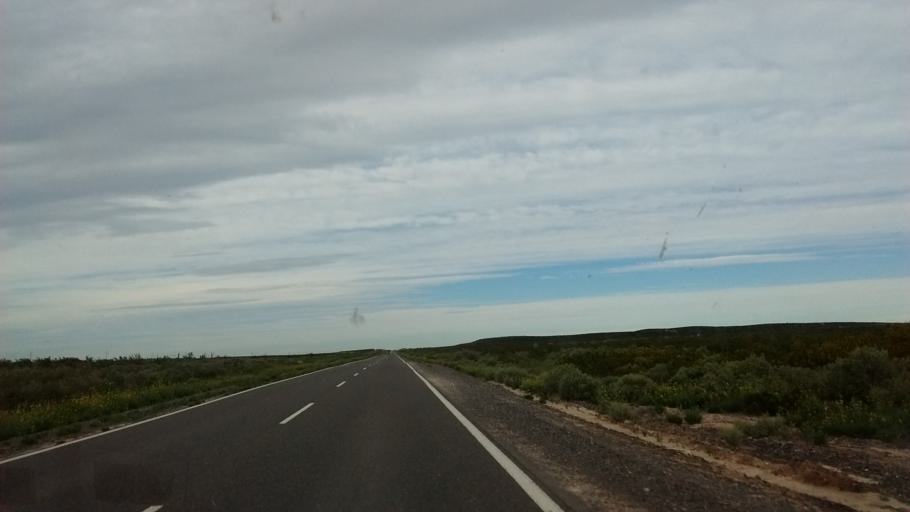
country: AR
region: Rio Negro
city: Contraalmirante Cordero
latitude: -38.4452
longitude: -68.0421
